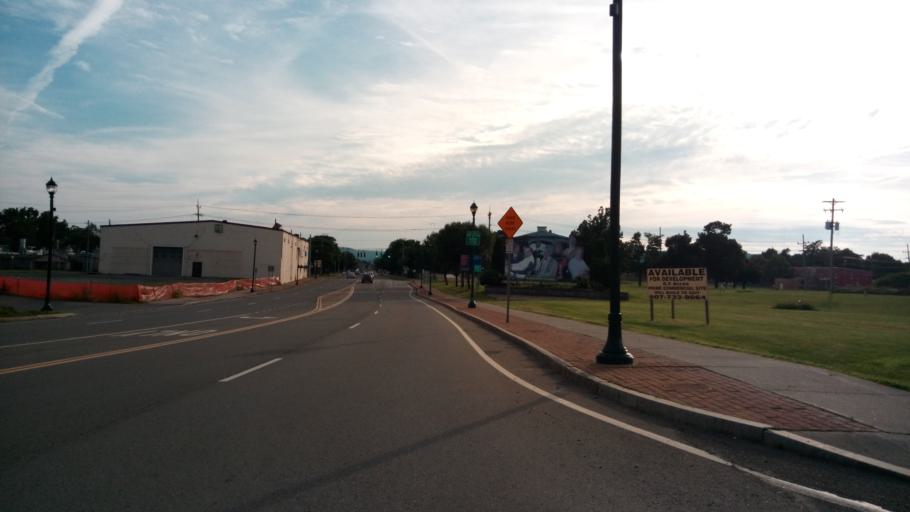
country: US
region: New York
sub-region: Chemung County
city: Elmira
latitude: 42.0954
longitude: -76.7899
